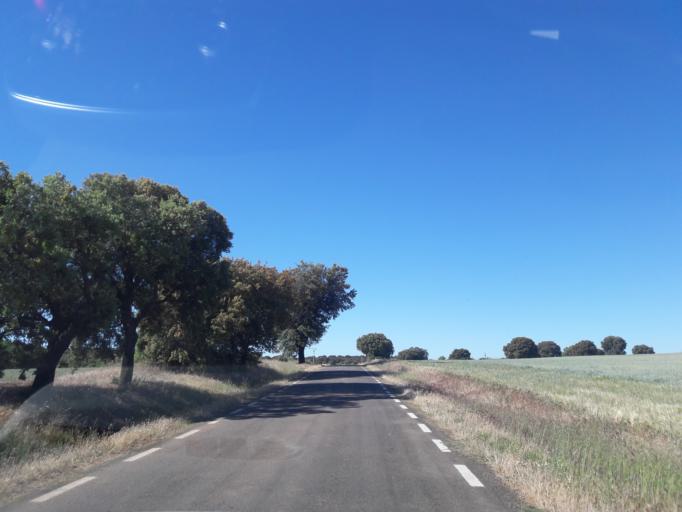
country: ES
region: Castille and Leon
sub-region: Provincia de Salamanca
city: Florida de Liebana
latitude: 41.0119
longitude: -5.7704
